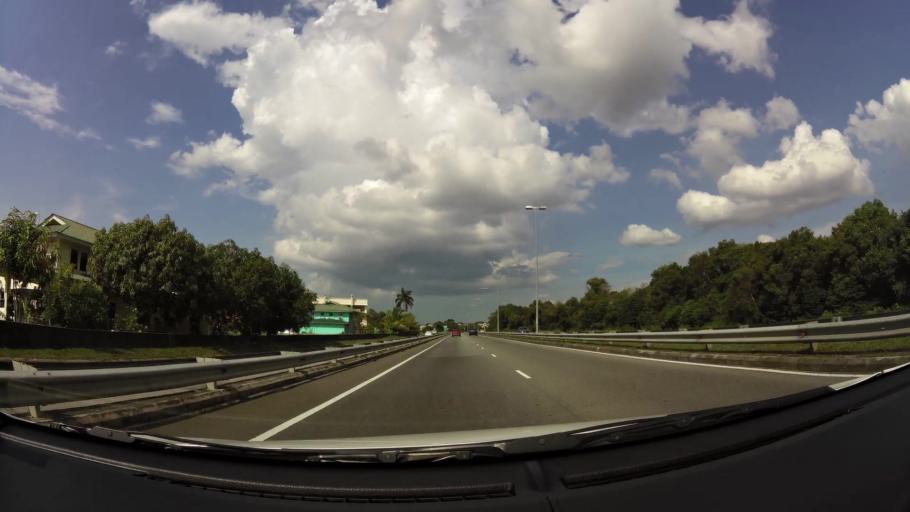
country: BN
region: Brunei and Muara
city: Bandar Seri Begawan
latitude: 4.9524
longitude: 114.9532
